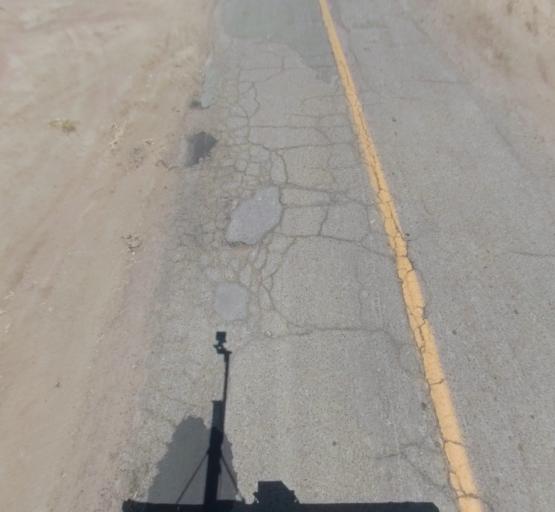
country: US
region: California
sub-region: Madera County
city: Chowchilla
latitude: 37.0979
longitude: -120.3651
